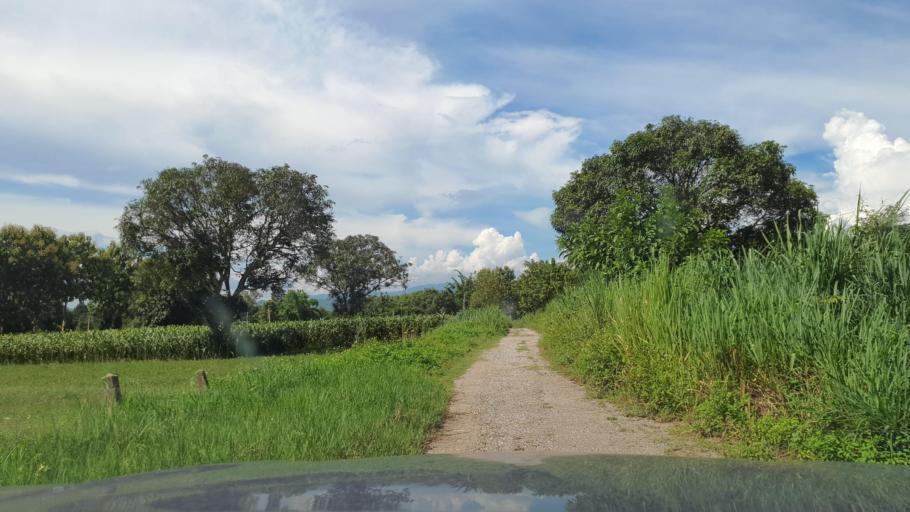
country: TH
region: Chiang Mai
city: Mae On
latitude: 18.7428
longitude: 99.2524
